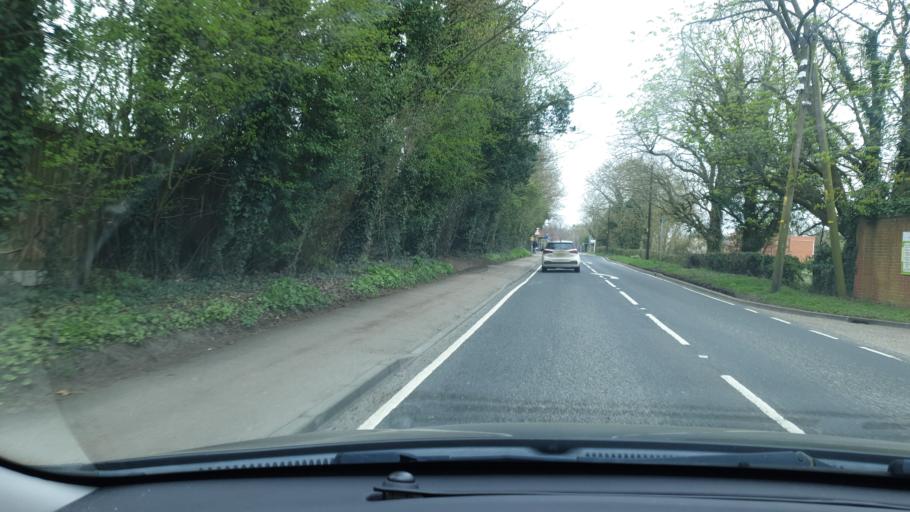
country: GB
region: England
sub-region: Essex
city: Great Horkesley
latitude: 51.9272
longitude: 0.8801
